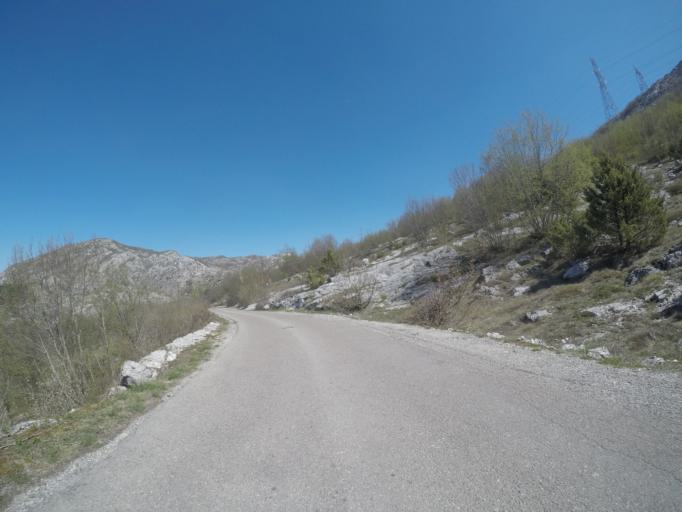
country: ME
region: Cetinje
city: Cetinje
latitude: 42.4543
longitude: 18.8737
